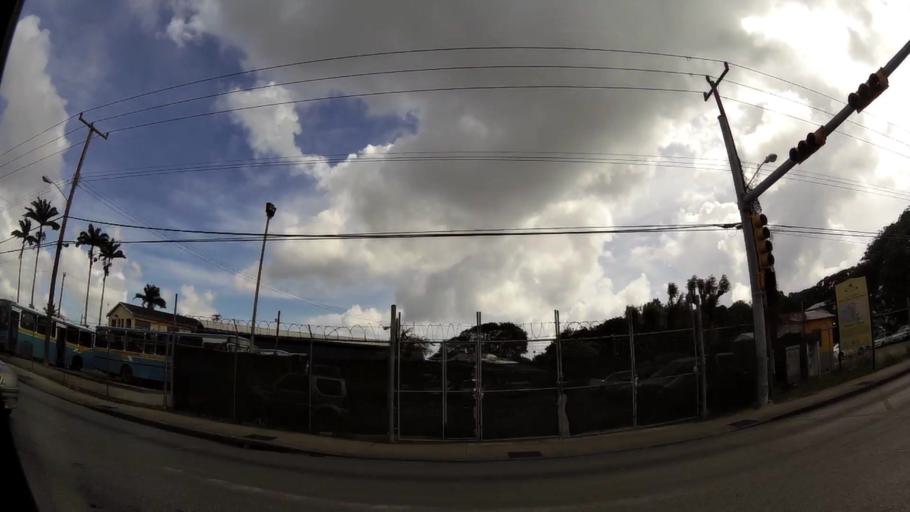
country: BB
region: Saint Michael
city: Bridgetown
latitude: 13.1023
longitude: -59.6104
